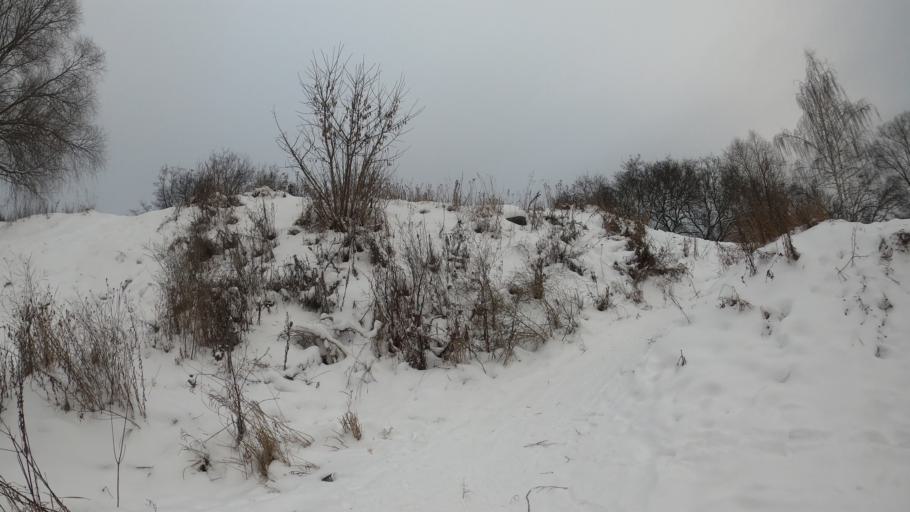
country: RU
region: Moskovskaya
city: Dolgoprudnyy
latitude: 55.9424
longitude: 37.4813
